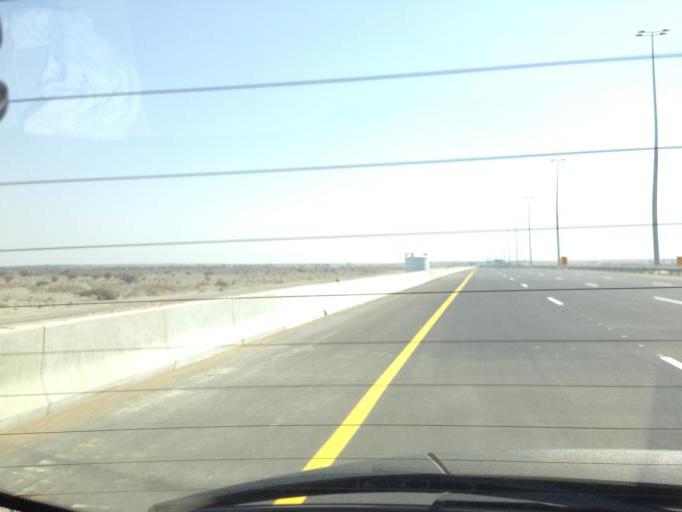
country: OM
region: Al Batinah
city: Rustaq
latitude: 23.5357
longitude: 57.5427
